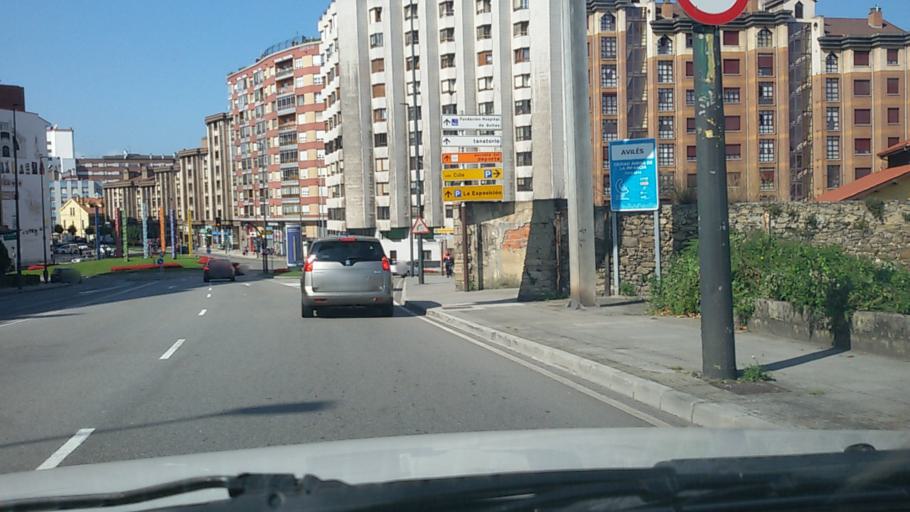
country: ES
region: Asturias
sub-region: Province of Asturias
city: Aviles
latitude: 43.5524
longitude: -5.9162
